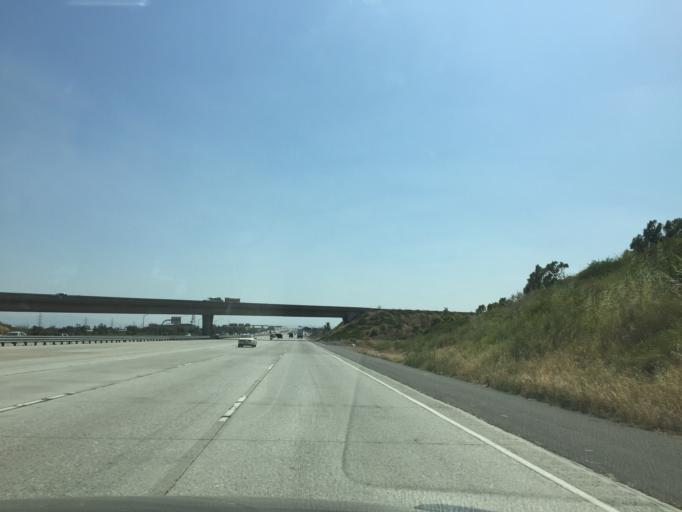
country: US
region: California
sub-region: San Bernardino County
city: Fontana
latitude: 34.1359
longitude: -117.4968
